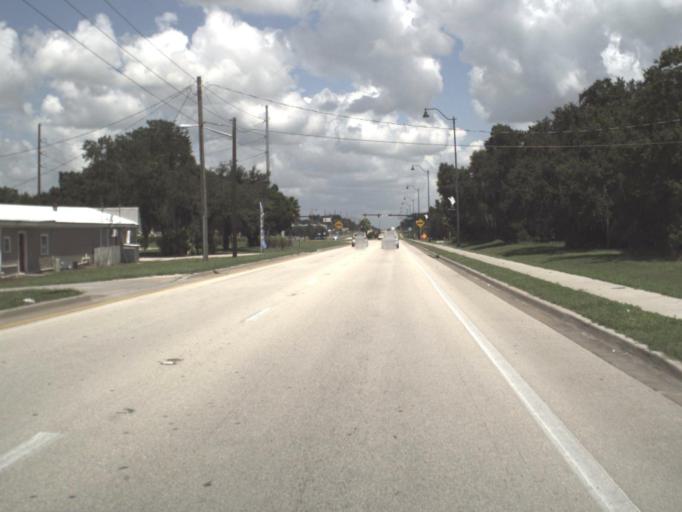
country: US
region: Florida
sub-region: Hardee County
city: Wauchula
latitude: 27.5551
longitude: -81.8123
